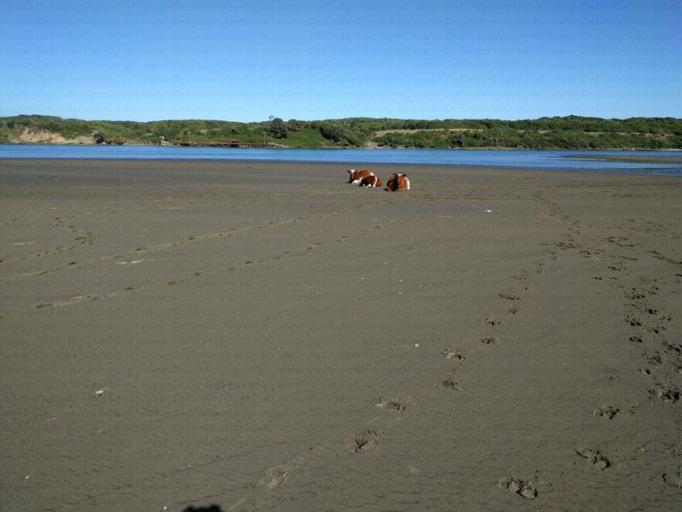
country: CL
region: Los Lagos
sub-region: Provincia de Chiloe
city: Ancud
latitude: -42.0480
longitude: -74.0215
